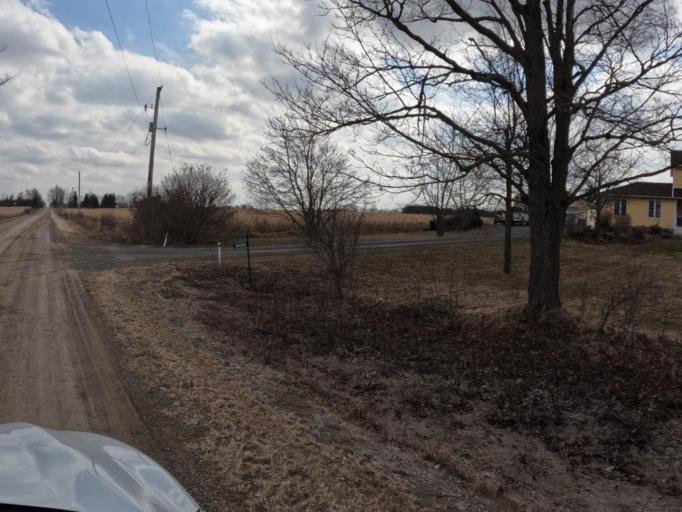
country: CA
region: Ontario
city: Shelburne
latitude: 43.9656
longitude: -80.2829
